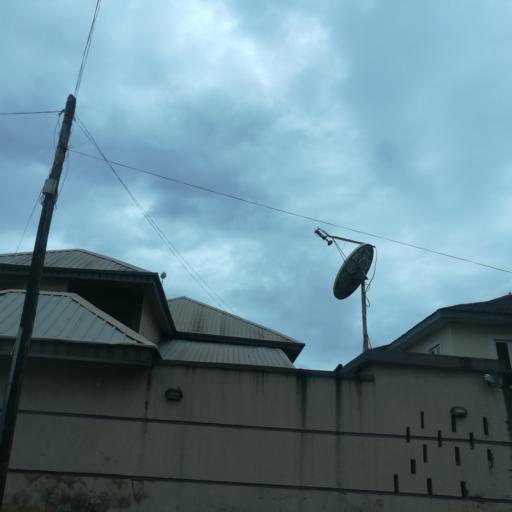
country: NG
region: Lagos
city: Ikoyi
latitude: 6.4470
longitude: 3.4561
